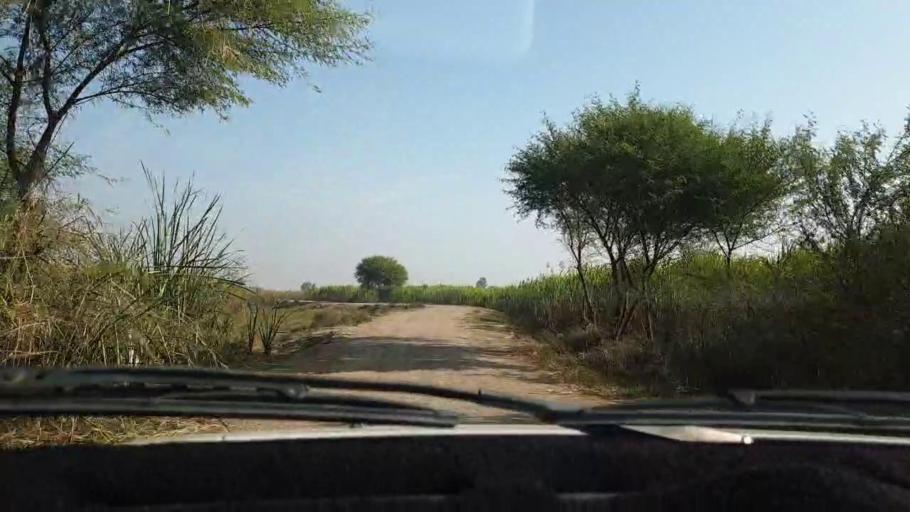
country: PK
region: Sindh
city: Tando Muhammad Khan
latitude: 25.0254
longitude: 68.4860
